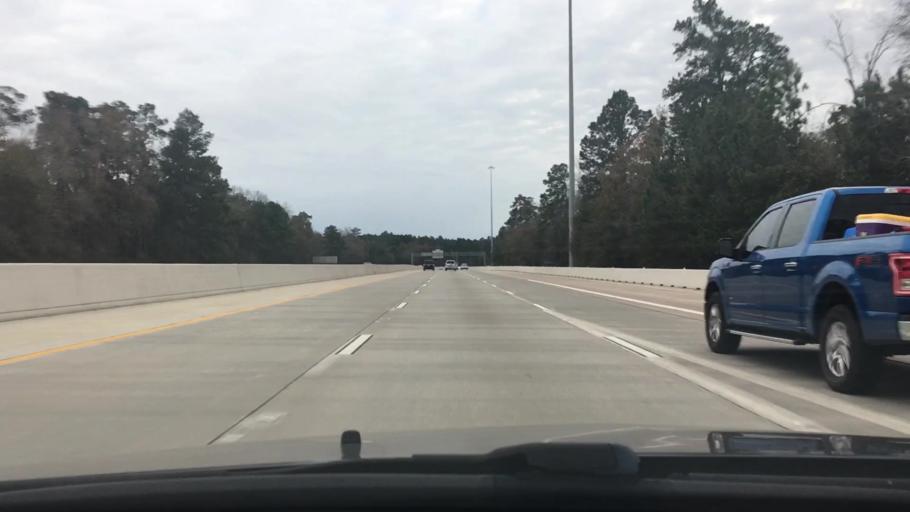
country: US
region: Texas
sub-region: Harris County
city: Spring
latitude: 30.0836
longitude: -95.4118
